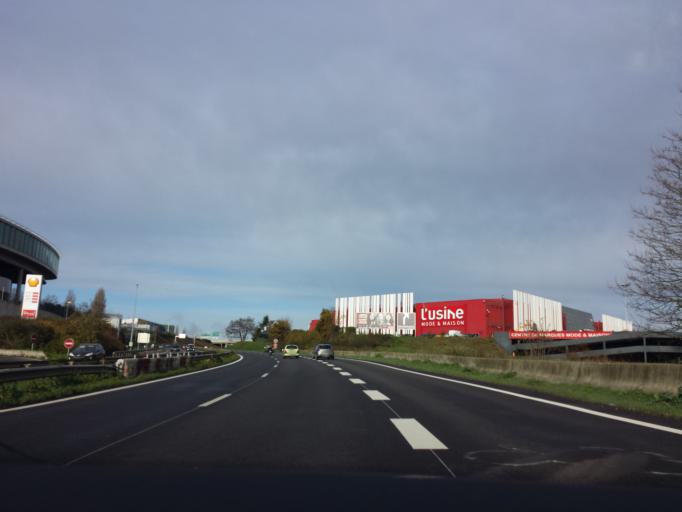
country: FR
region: Ile-de-France
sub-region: Departement de l'Essonne
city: Bievres
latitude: 48.7715
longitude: 2.2284
